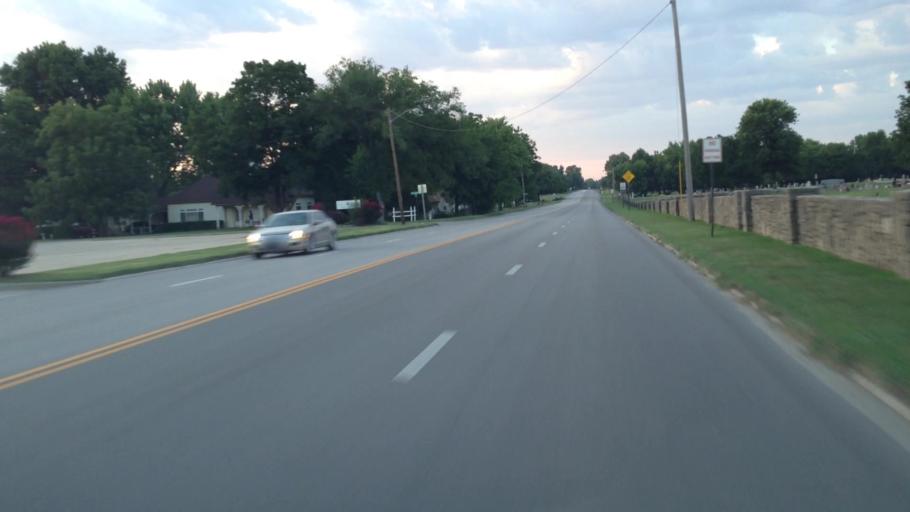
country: US
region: Kansas
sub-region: Montgomery County
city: Independence
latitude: 37.2464
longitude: -95.7062
